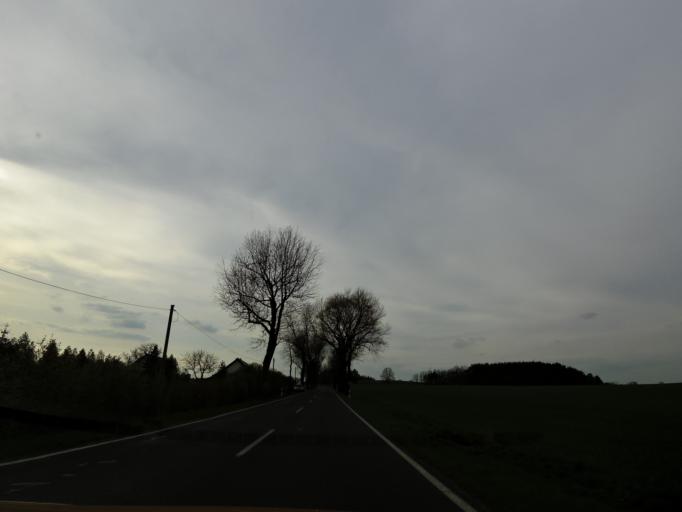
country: DE
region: Brandenburg
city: Mittenwalde
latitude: 52.2534
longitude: 13.5541
